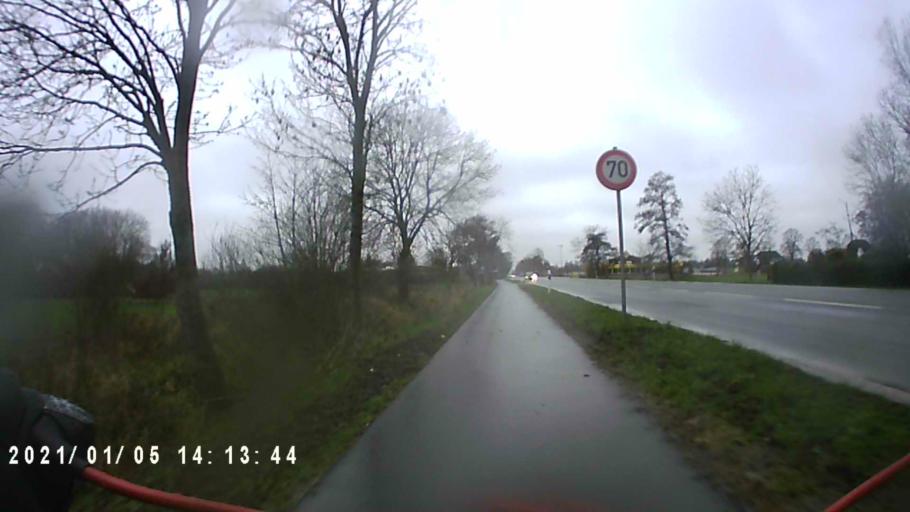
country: DE
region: Lower Saxony
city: Weener
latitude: 53.1721
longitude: 7.3209
